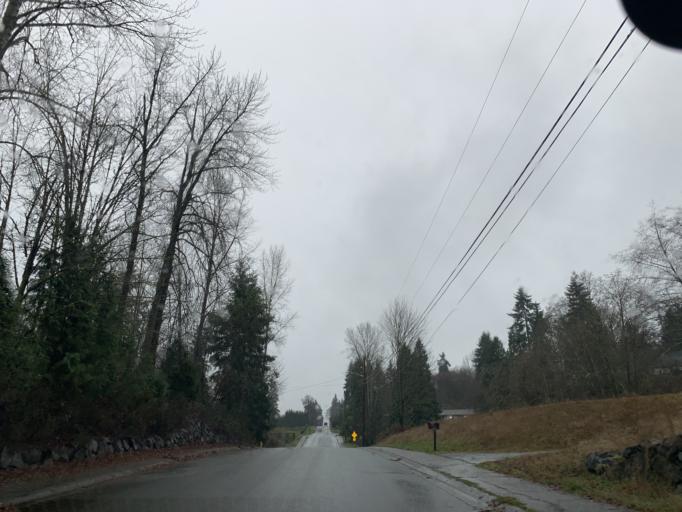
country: US
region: Washington
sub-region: King County
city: Woodinville
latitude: 47.7374
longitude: -122.1637
